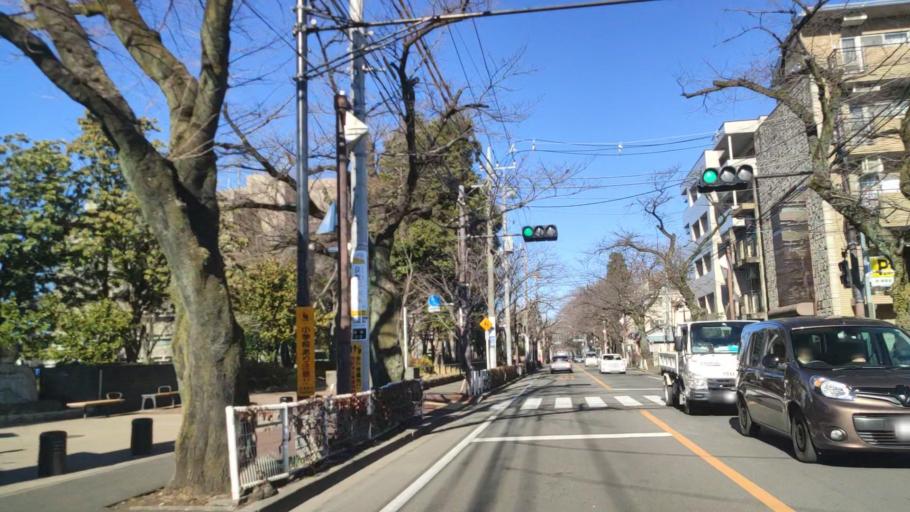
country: JP
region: Tokyo
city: Musashino
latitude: 35.7163
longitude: 139.5658
